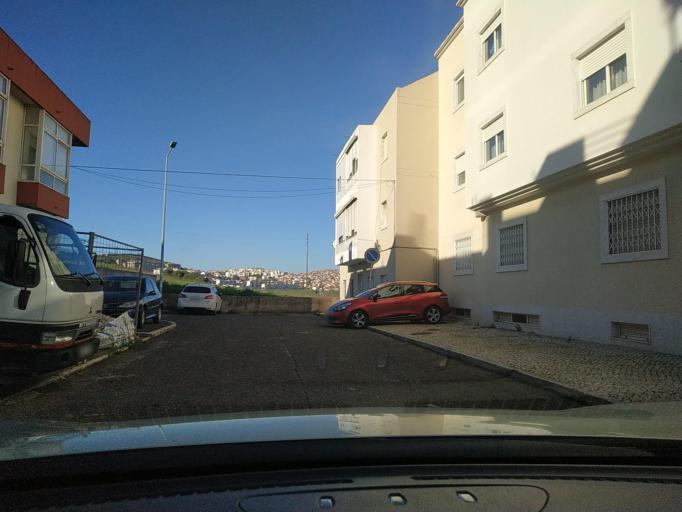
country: PT
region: Lisbon
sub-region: Odivelas
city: Famoes
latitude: 38.7702
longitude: -9.2191
